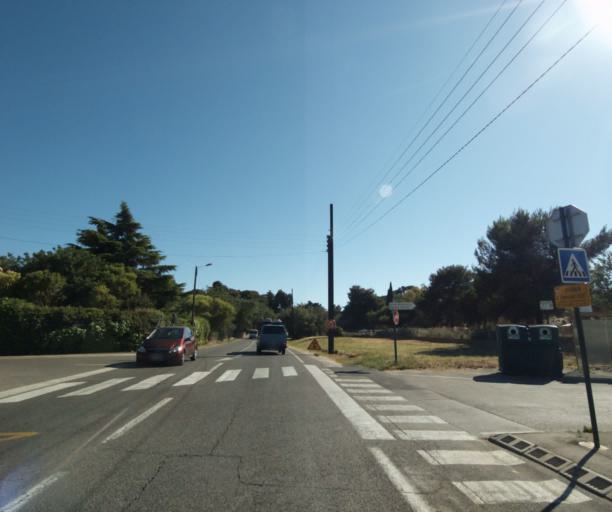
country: FR
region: Provence-Alpes-Cote d'Azur
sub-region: Departement du Var
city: La Garde
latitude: 43.1085
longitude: 5.9986
